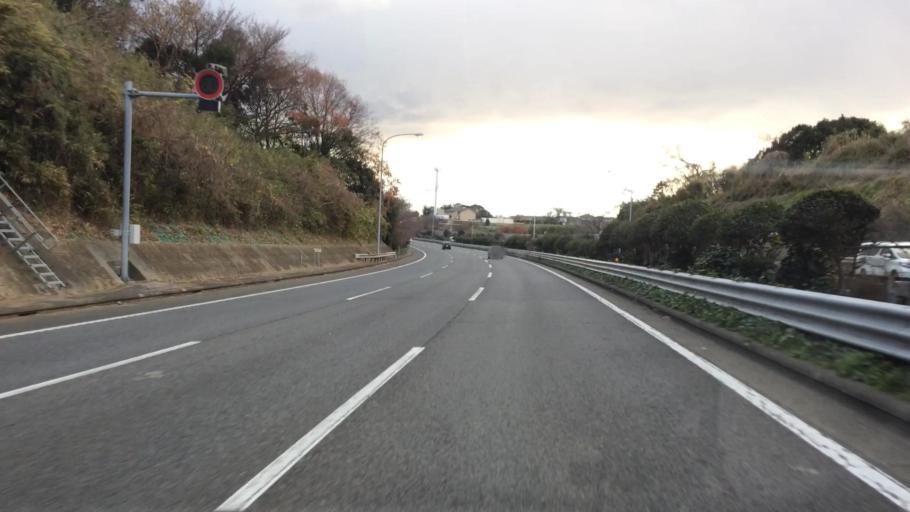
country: JP
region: Kanagawa
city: Yokohama
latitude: 35.4987
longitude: 139.5914
